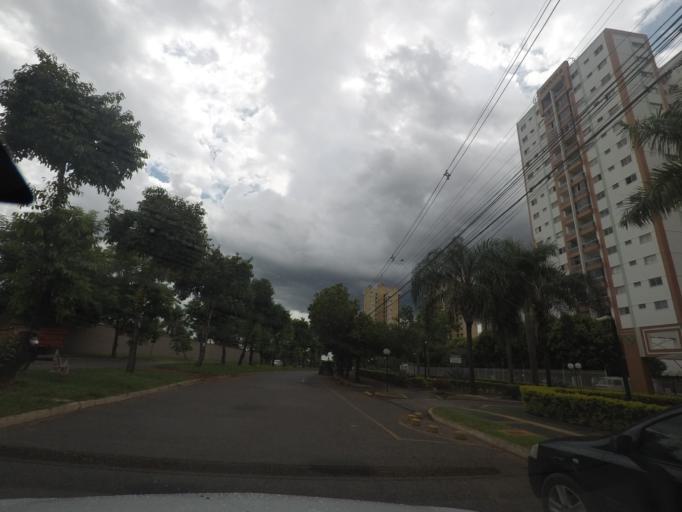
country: BR
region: Goias
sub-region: Goiania
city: Goiania
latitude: -16.7106
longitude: -49.3299
